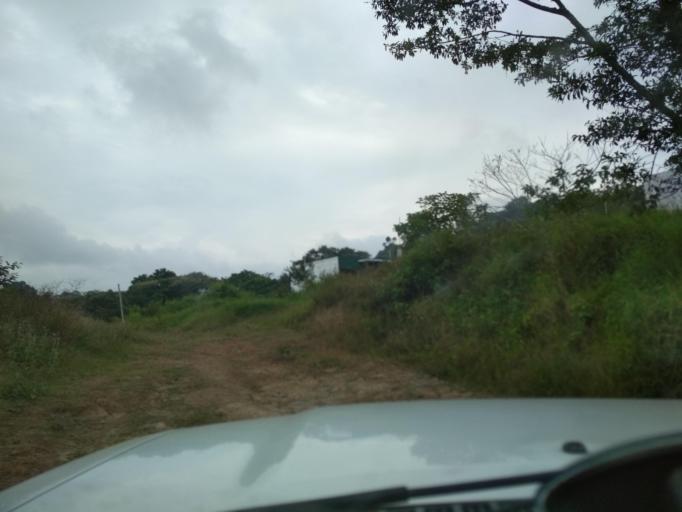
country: MX
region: Veracruz
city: El Castillo
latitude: 19.5651
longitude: -96.8681
